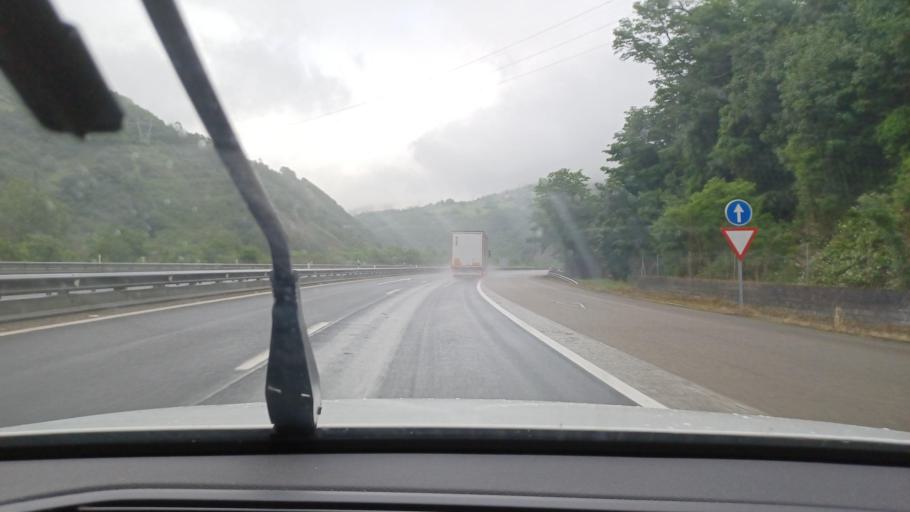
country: ES
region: Asturias
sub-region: Province of Asturias
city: Pola de Lena
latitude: 43.1844
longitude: -5.8076
